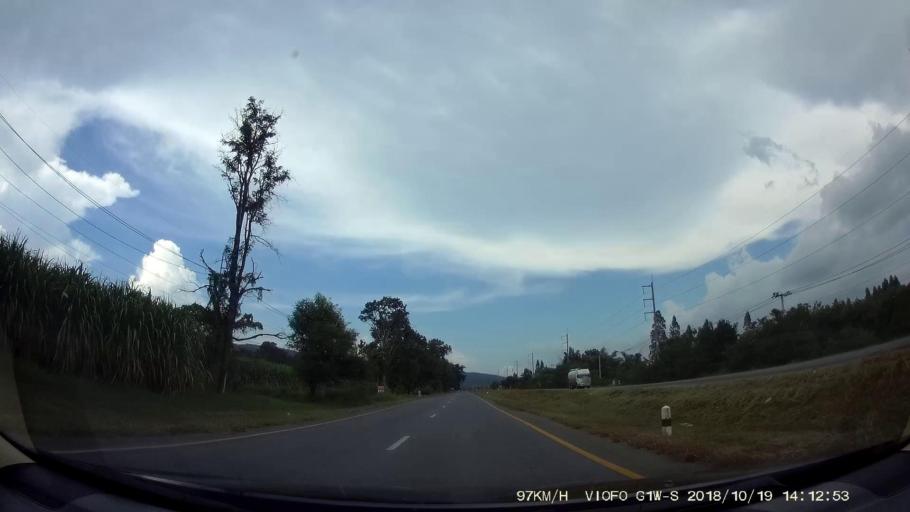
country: TH
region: Chaiyaphum
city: Khon Sawan
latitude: 15.9537
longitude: 102.1775
